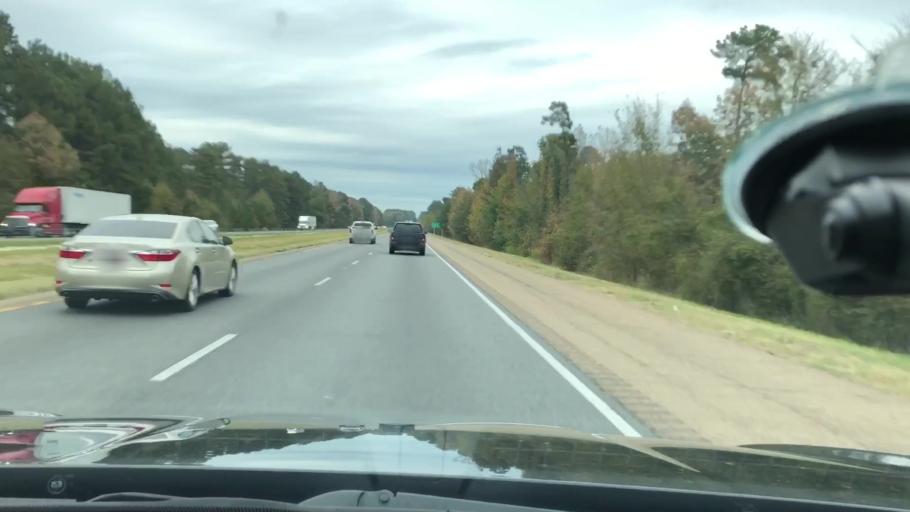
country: US
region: Arkansas
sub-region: Clark County
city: Gurdon
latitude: 33.9091
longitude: -93.2889
